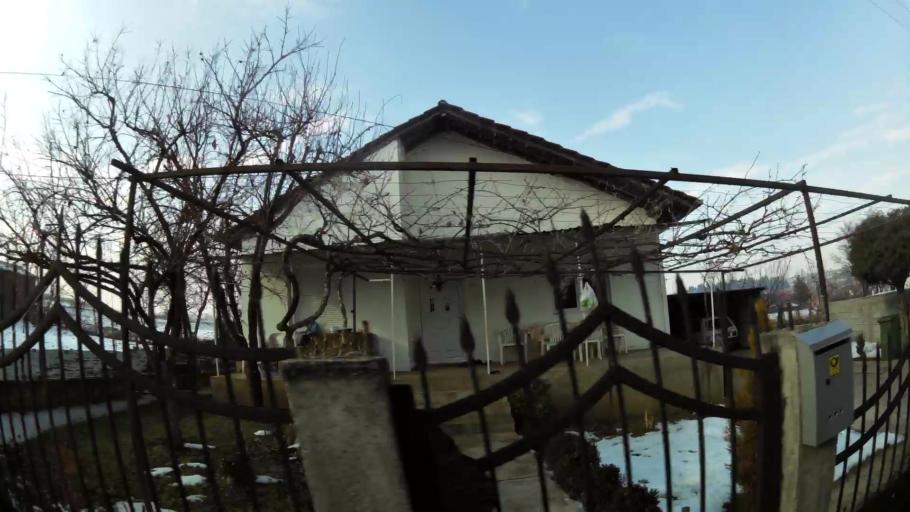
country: MK
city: Creshevo
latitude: 42.0110
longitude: 21.4959
